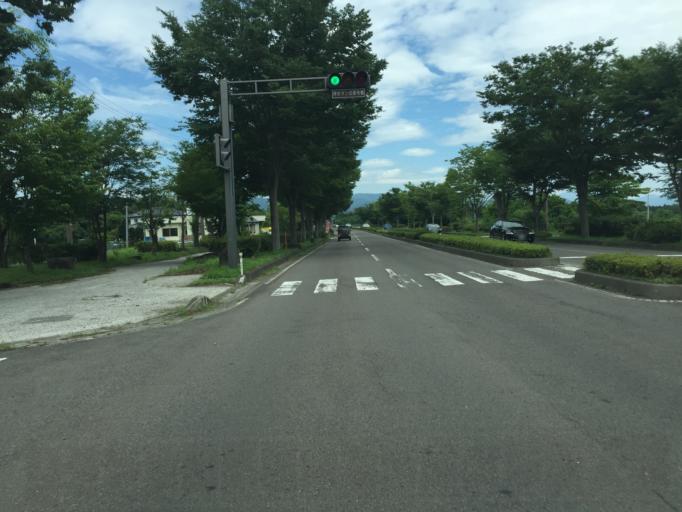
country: JP
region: Fukushima
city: Fukushima-shi
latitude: 37.7316
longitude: 140.3863
